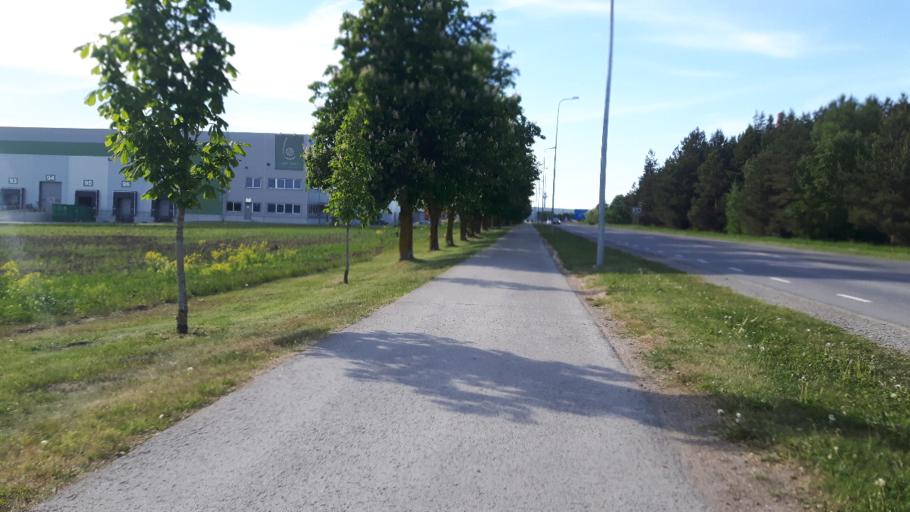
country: EE
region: Harju
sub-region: Joelaehtme vald
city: Loo
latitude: 59.4400
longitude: 24.9353
